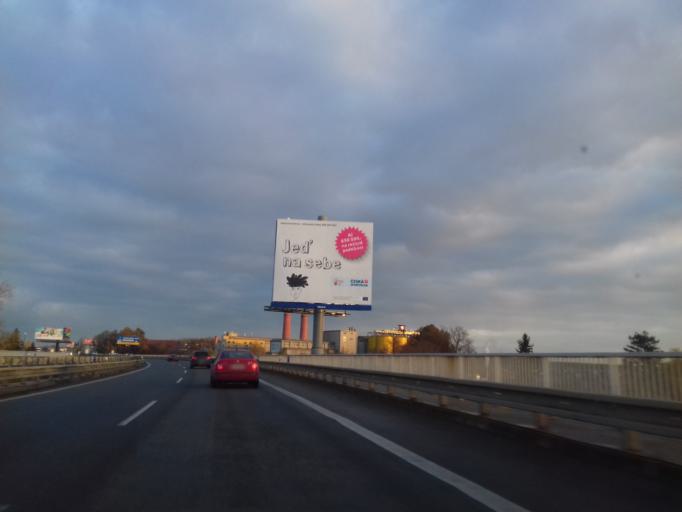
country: CZ
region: Olomoucky
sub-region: Okres Prostejov
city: Prostejov
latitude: 49.4720
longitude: 17.1338
